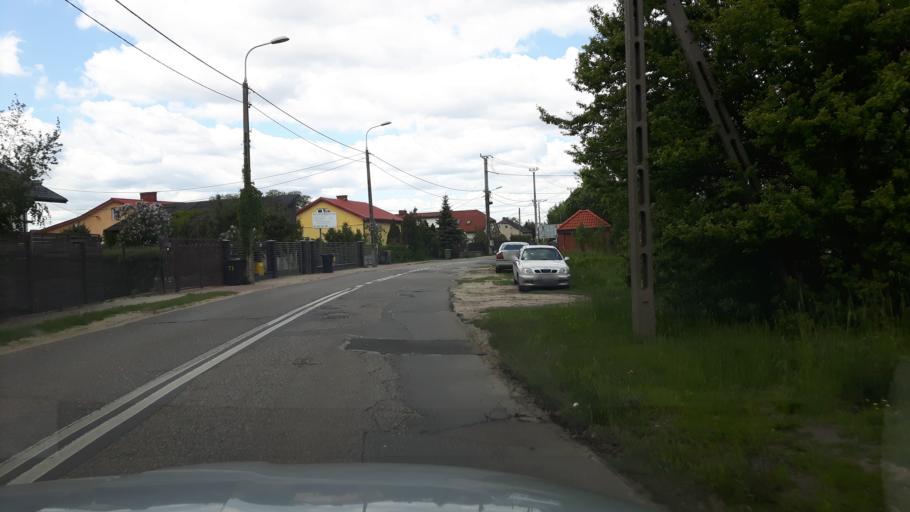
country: PL
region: Masovian Voivodeship
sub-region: Warszawa
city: Targowek
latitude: 52.3313
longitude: 21.0563
